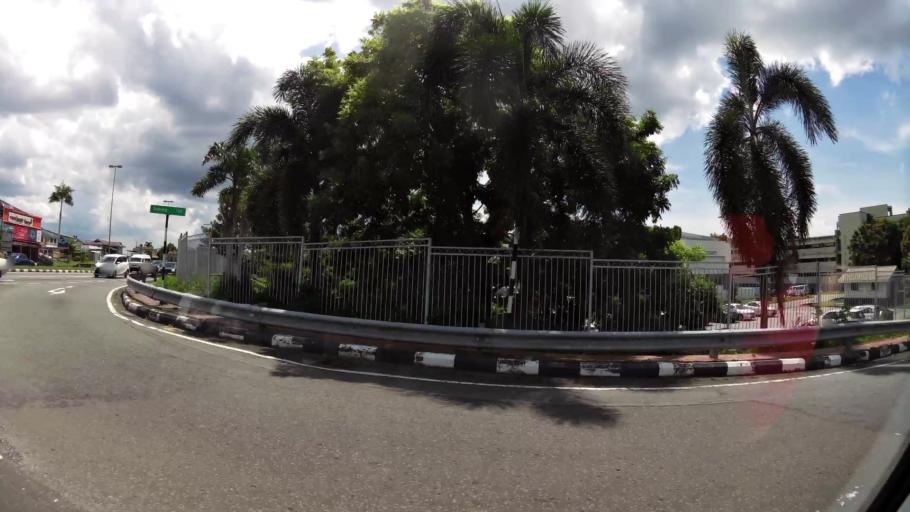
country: BN
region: Brunei and Muara
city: Bandar Seri Begawan
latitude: 4.9457
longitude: 114.9512
